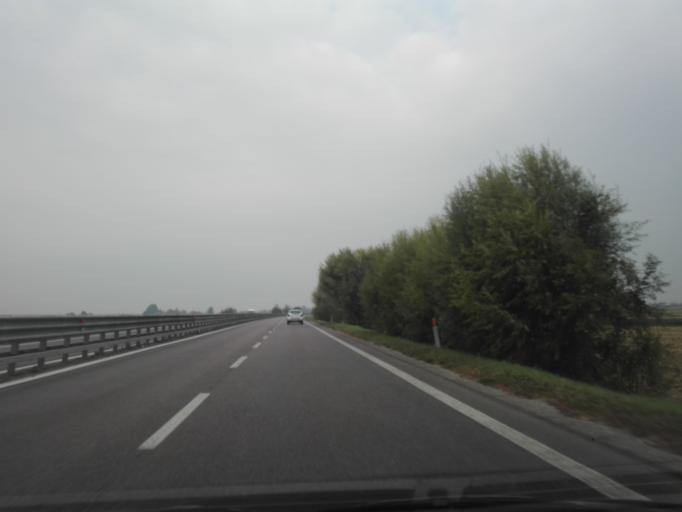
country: IT
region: Veneto
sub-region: Provincia di Verona
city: Villa Bartolomea
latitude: 45.1541
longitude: 11.3278
